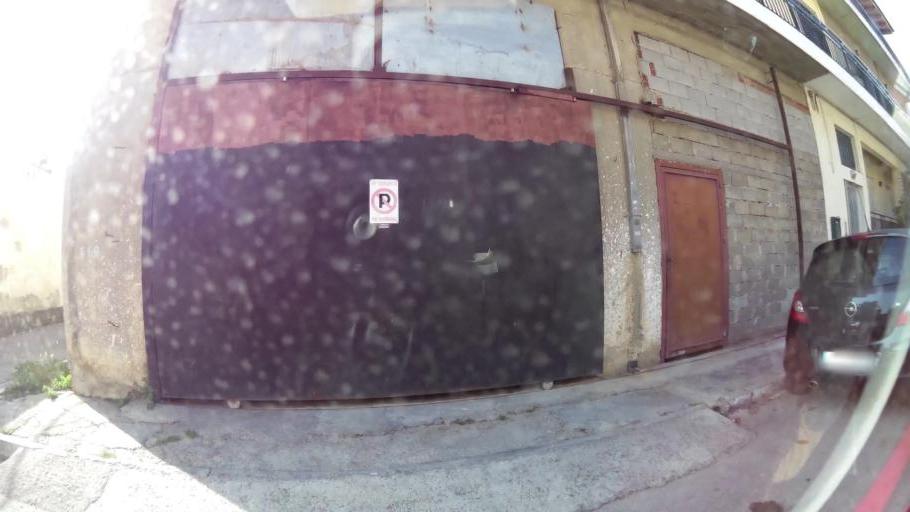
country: GR
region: Attica
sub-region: Nomarchia Dytikis Attikis
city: Zefyri
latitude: 38.0716
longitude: 23.7130
